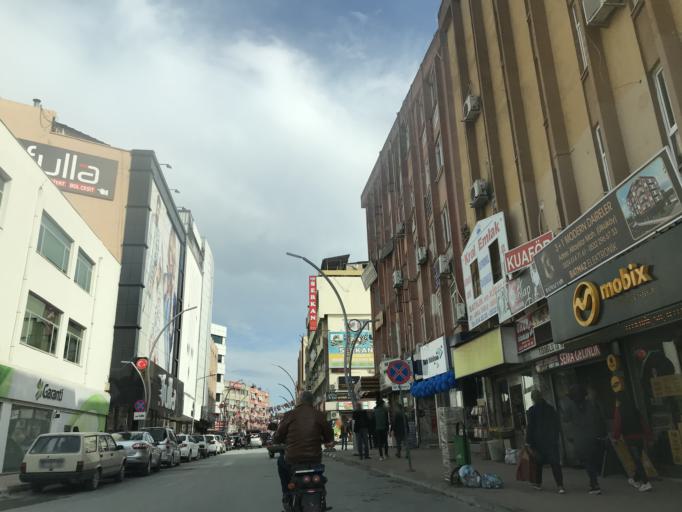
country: TR
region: Mersin
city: Tarsus
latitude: 36.9167
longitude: 34.8920
